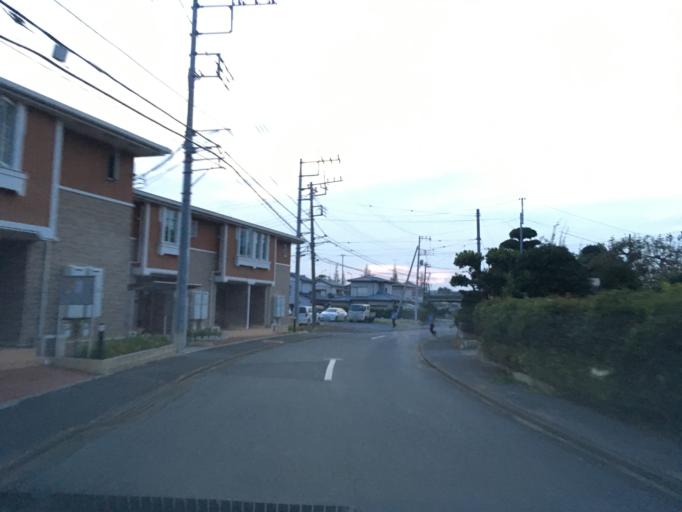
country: JP
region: Chiba
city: Kimitsu
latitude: 35.3443
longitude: 139.9121
